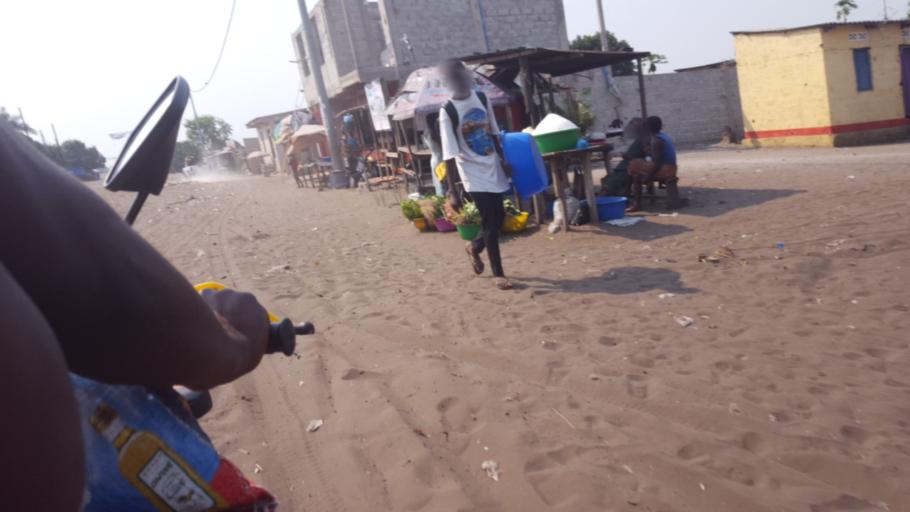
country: CD
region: Kinshasa
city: Masina
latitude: -4.3625
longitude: 15.5096
